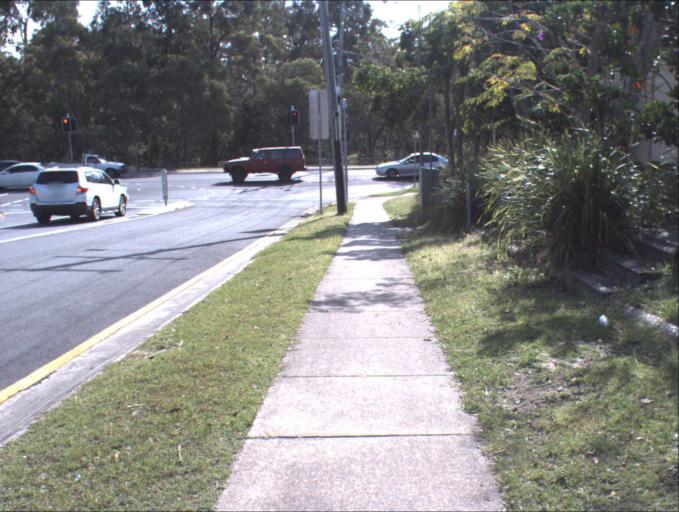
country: AU
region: Queensland
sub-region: Brisbane
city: Sunnybank Hills
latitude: -27.6672
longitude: 153.0526
